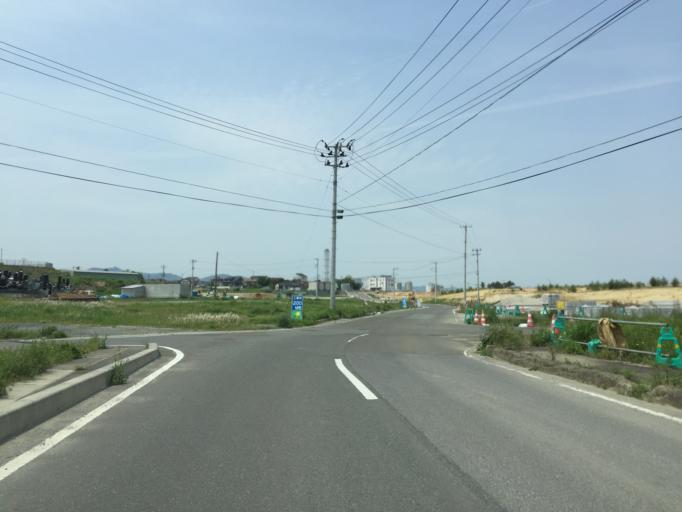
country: JP
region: Miyagi
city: Marumori
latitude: 37.8257
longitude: 140.9669
